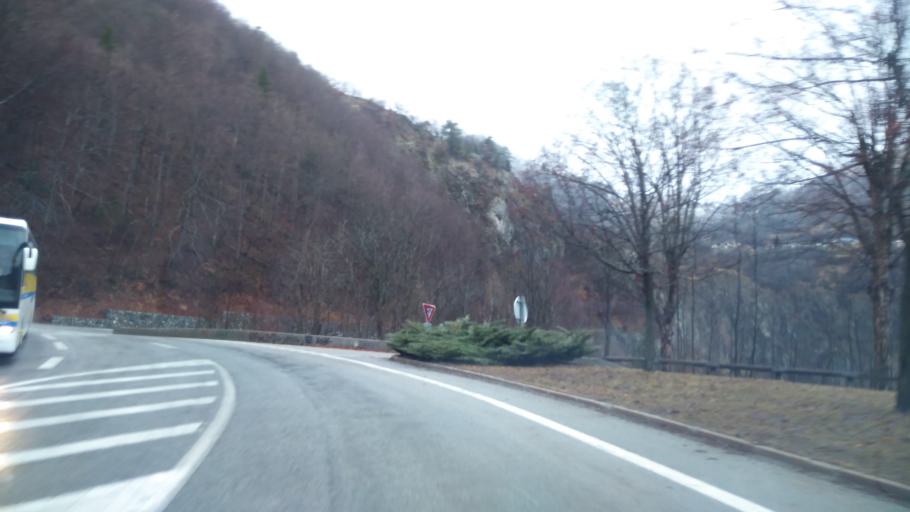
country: FR
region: Rhone-Alpes
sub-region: Departement de l'Isere
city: Mont-de-Lans
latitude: 45.0389
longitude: 6.1025
